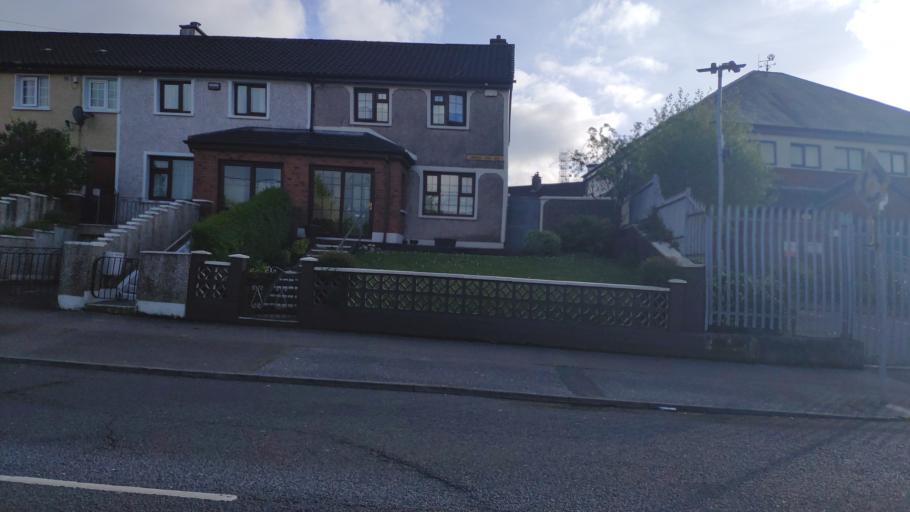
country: IE
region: Munster
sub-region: County Cork
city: Cork
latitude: 51.9147
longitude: -8.4845
